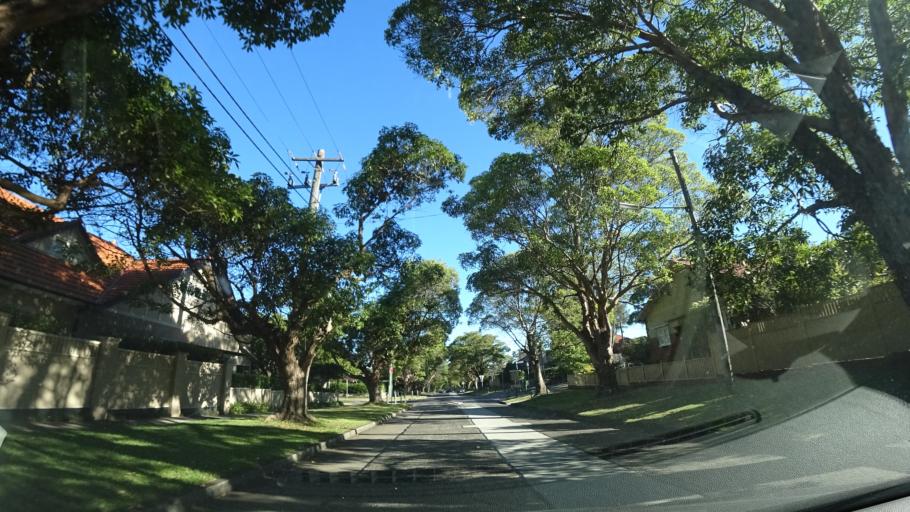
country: AU
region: New South Wales
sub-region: Ku-ring-gai
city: Roseville Chase
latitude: -33.7876
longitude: 151.1894
